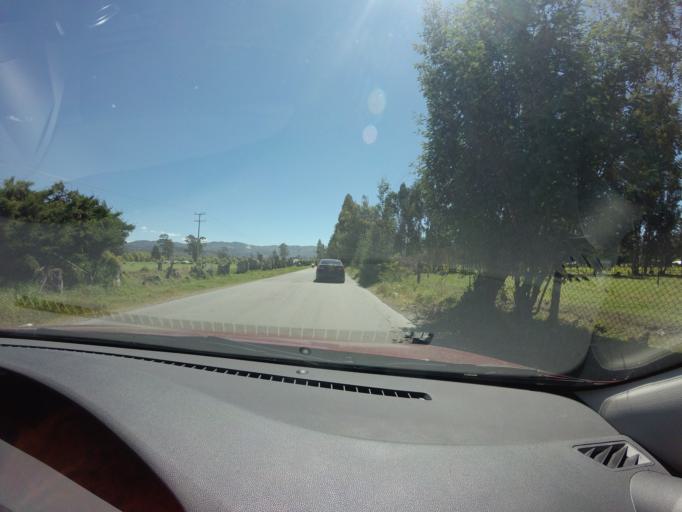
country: CO
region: Cundinamarca
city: Ubate
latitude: 5.2964
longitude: -73.8138
